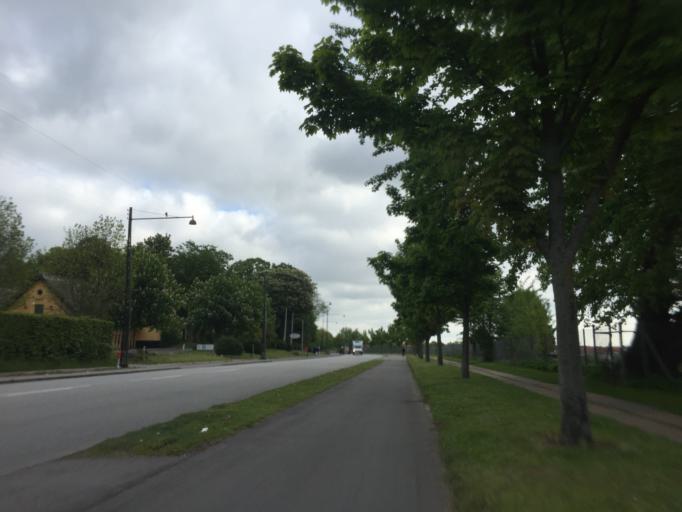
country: DK
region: Capital Region
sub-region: Kobenhavn
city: Vanlose
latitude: 55.7010
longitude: 12.5110
